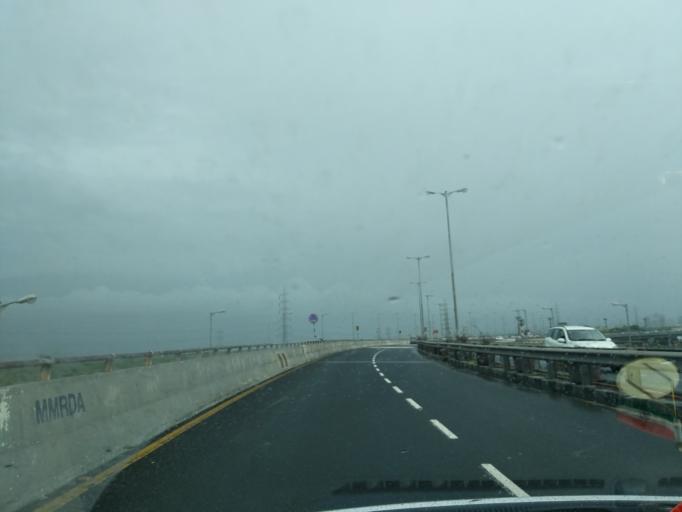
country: IN
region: Maharashtra
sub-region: Mumbai Suburban
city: Mumbai
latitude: 19.0135
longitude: 72.8716
